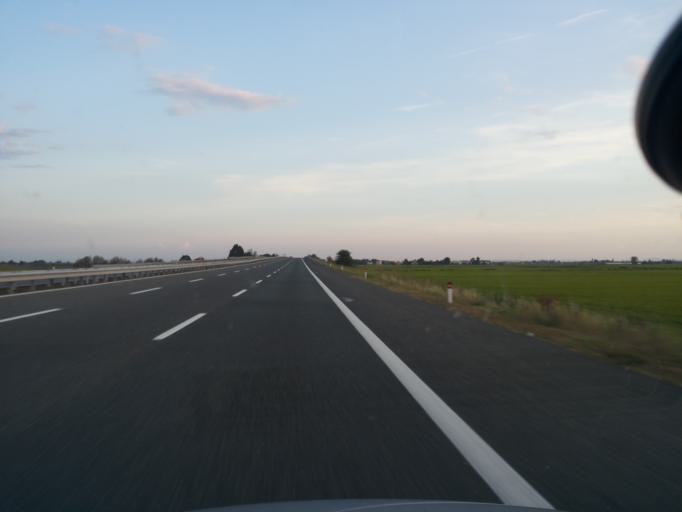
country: IT
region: Piedmont
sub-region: Provincia di Novara
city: Casalvolone
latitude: 45.3875
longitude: 8.4846
